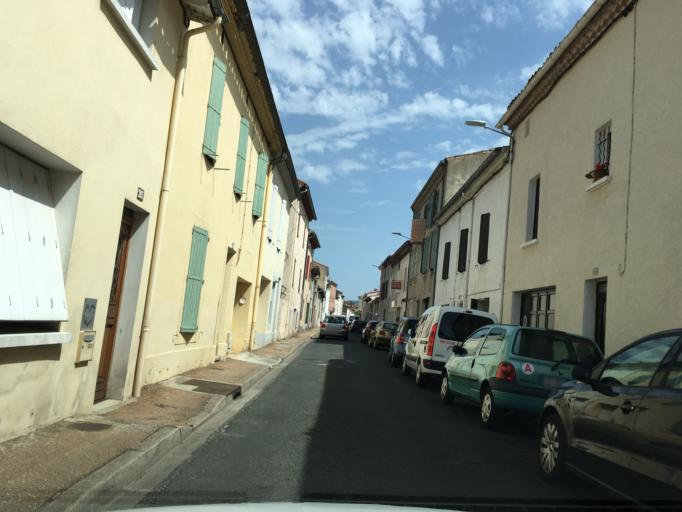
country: FR
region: Midi-Pyrenees
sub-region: Departement du Tarn
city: Castres
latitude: 43.6097
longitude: 2.2399
